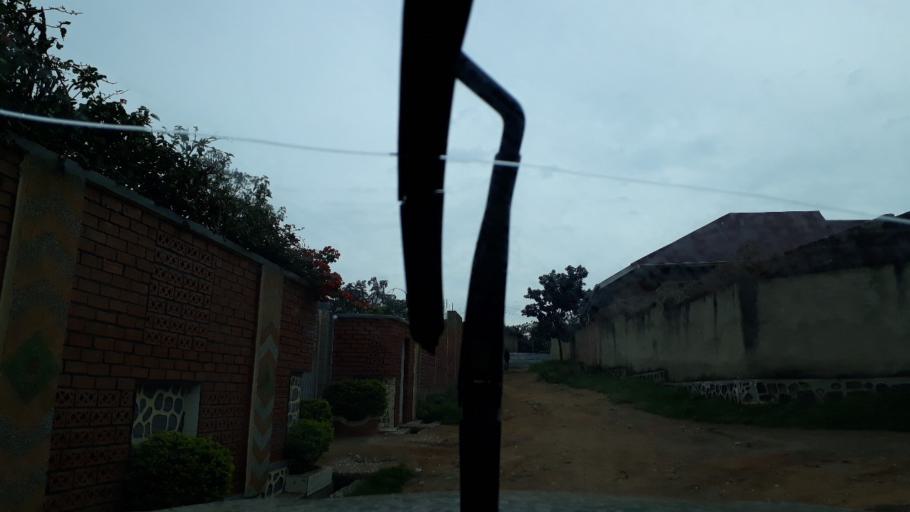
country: CD
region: Eastern Province
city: Bunia
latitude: 1.5627
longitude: 30.2419
